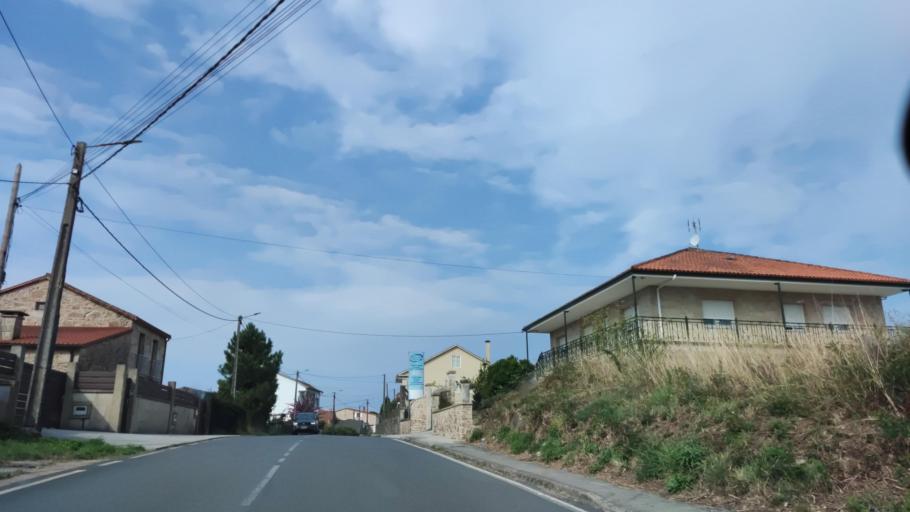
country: ES
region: Galicia
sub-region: Provincia da Coruna
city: Rianxo
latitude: 42.6477
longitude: -8.8063
